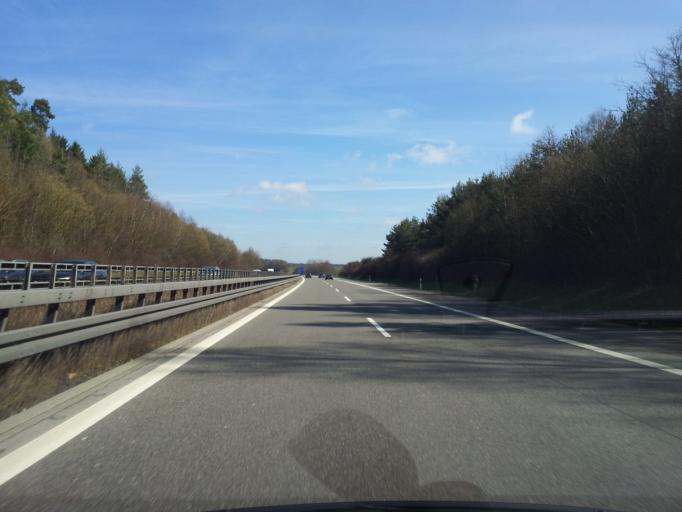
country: DE
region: Baden-Wuerttemberg
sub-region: Karlsruhe Region
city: Empfingen
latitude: 48.4226
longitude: 8.7382
